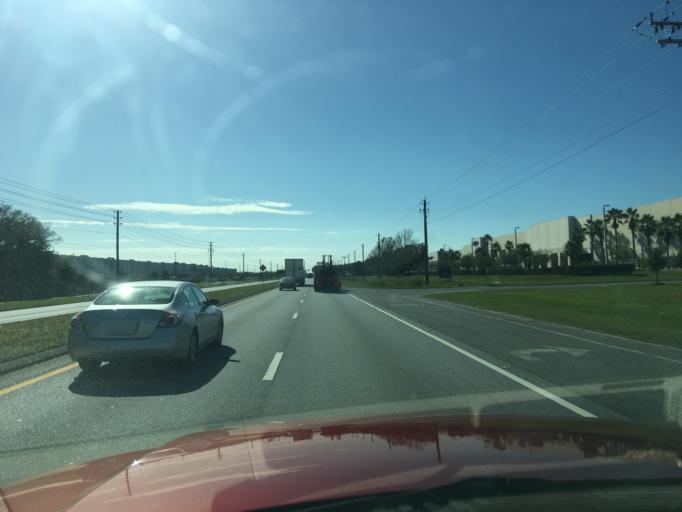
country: US
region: Florida
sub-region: Polk County
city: Winston
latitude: 28.0245
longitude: -82.0558
